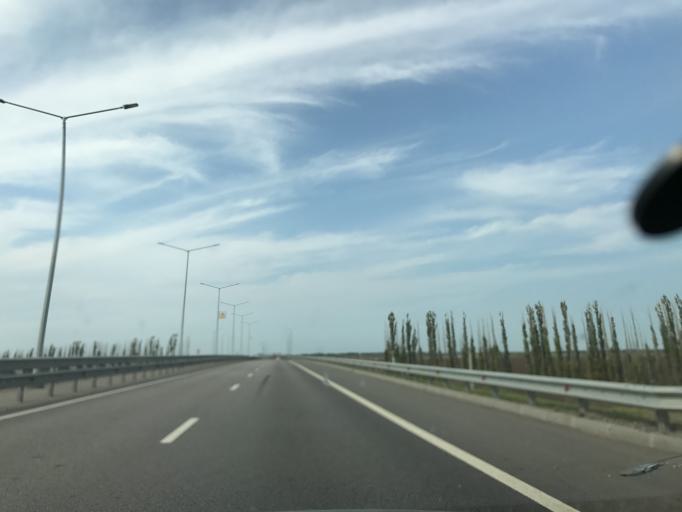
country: RU
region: Voronezj
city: Kashirskoye
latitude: 51.4810
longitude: 39.5475
